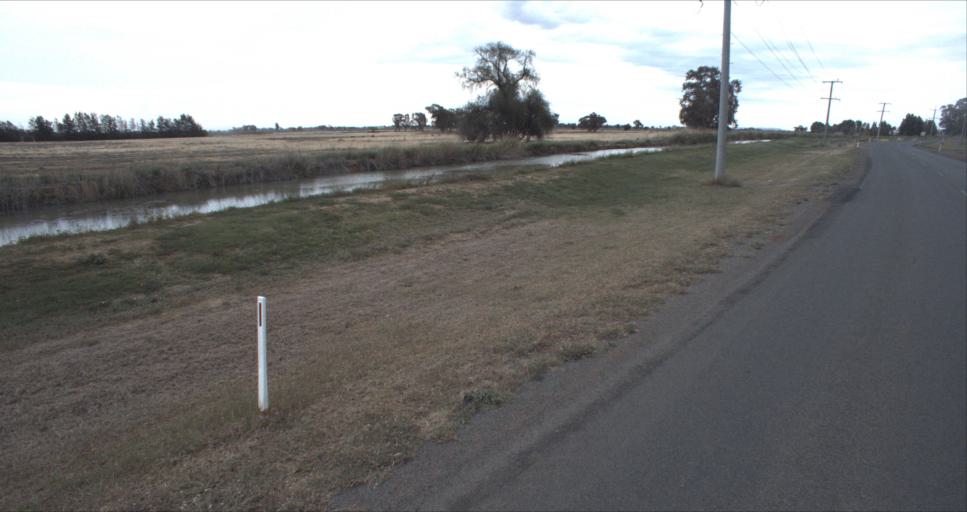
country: AU
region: New South Wales
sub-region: Leeton
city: Leeton
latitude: -34.5350
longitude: 146.3884
